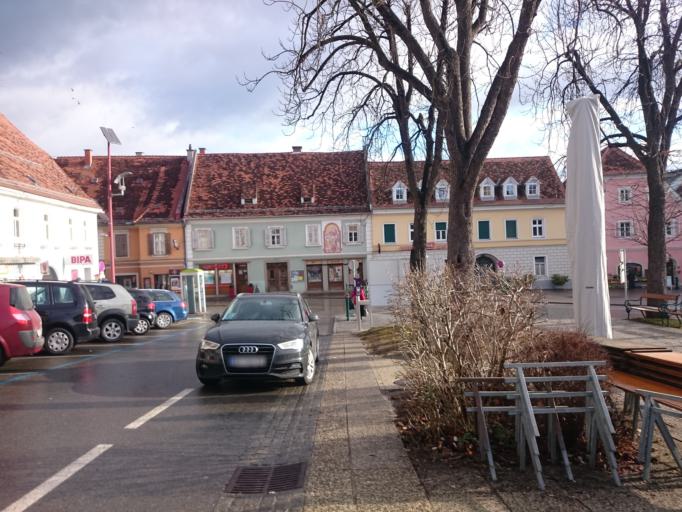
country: AT
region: Styria
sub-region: Politischer Bezirk Weiz
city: Weiz
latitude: 47.2174
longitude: 15.6223
